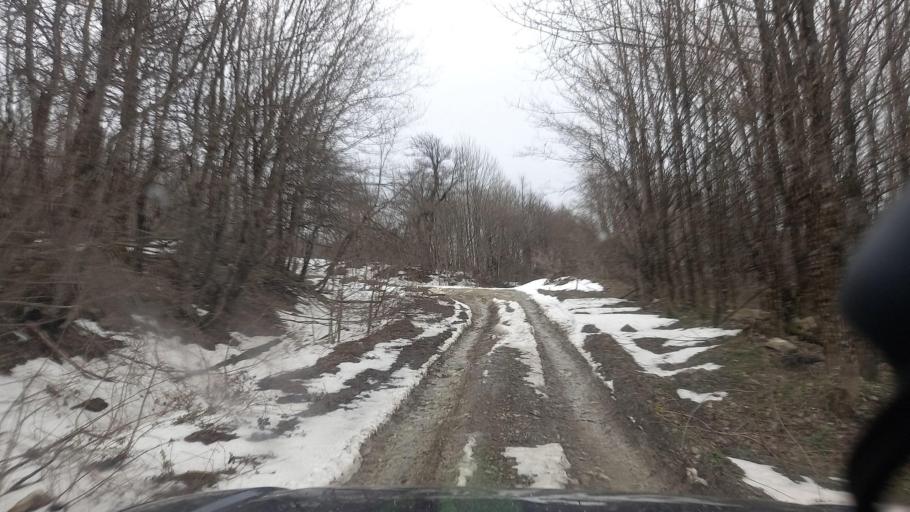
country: RU
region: Krasnodarskiy
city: Pshada
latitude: 44.5967
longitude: 38.3240
